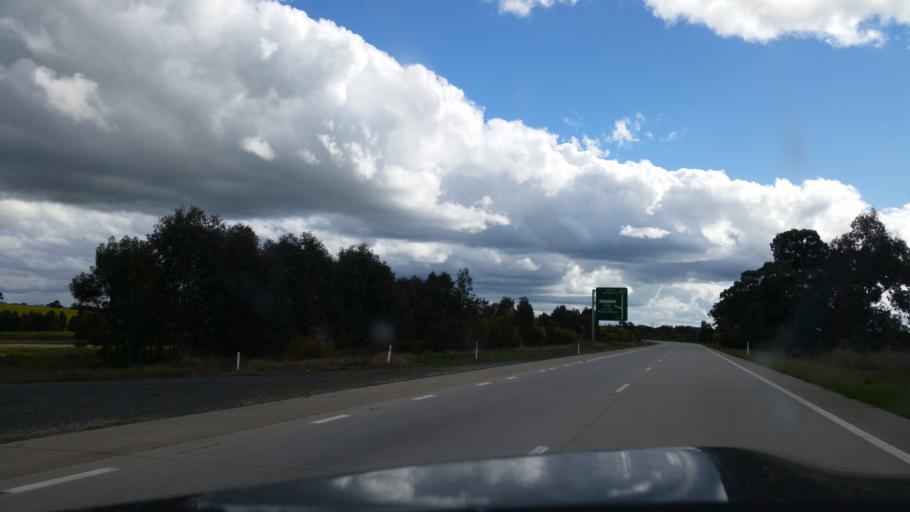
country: AU
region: New South Wales
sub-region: Greater Hume Shire
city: Jindera
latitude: -35.9249
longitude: 147.0164
